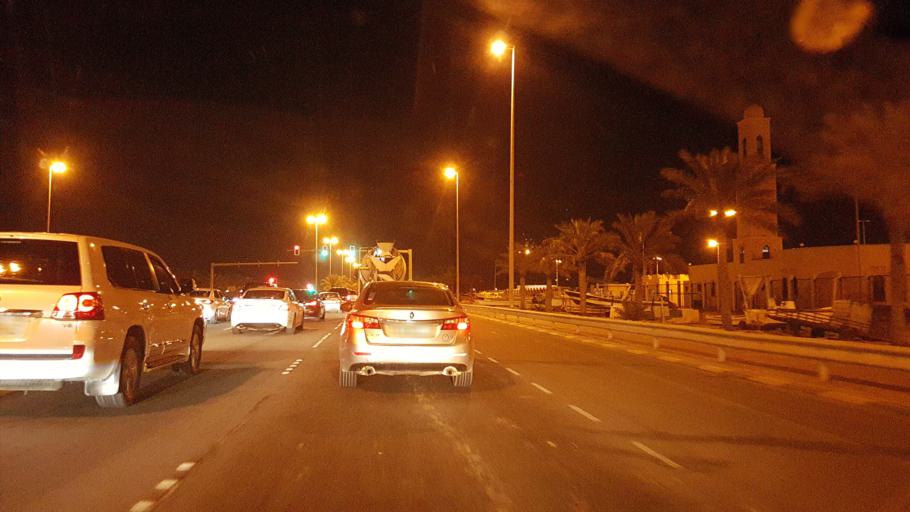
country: BH
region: Muharraq
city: Al Hadd
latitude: 26.2439
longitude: 50.6584
